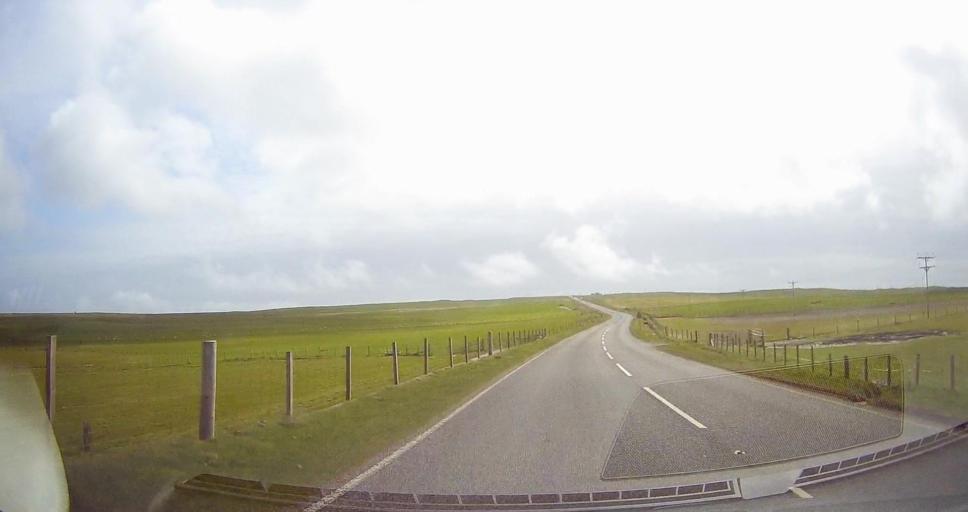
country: GB
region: Scotland
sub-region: Shetland Islands
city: Sandwick
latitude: 59.9098
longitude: -1.3014
